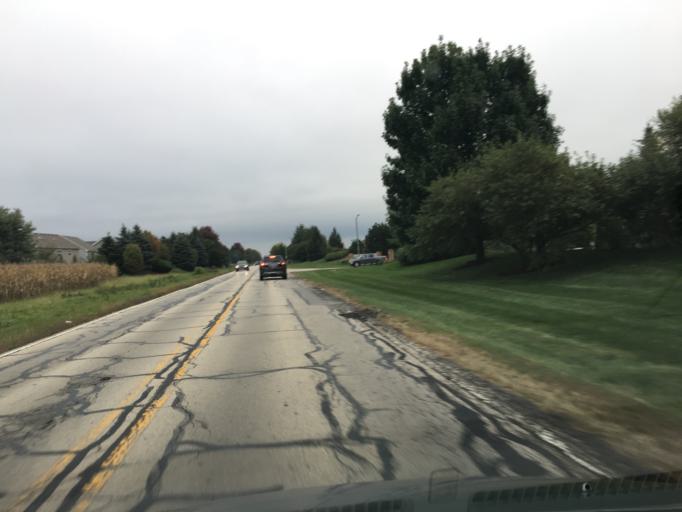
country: US
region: Illinois
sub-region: Will County
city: Plainfield
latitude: 41.6520
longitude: -88.1776
